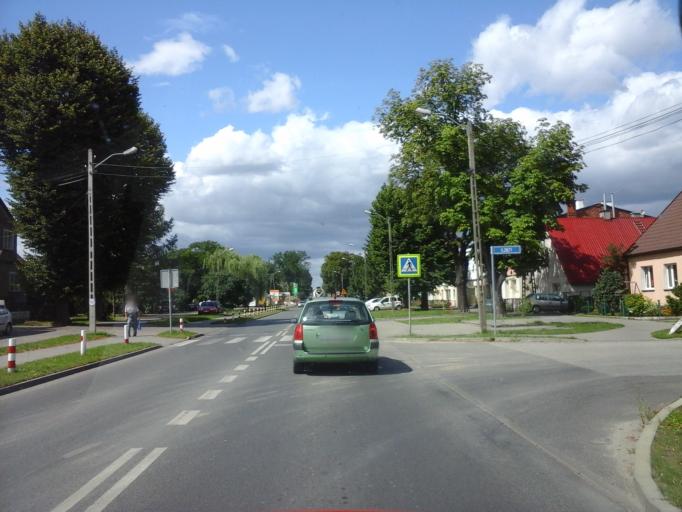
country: PL
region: West Pomeranian Voivodeship
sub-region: Powiat policki
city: Przeclaw
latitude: 53.4291
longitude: 14.4691
